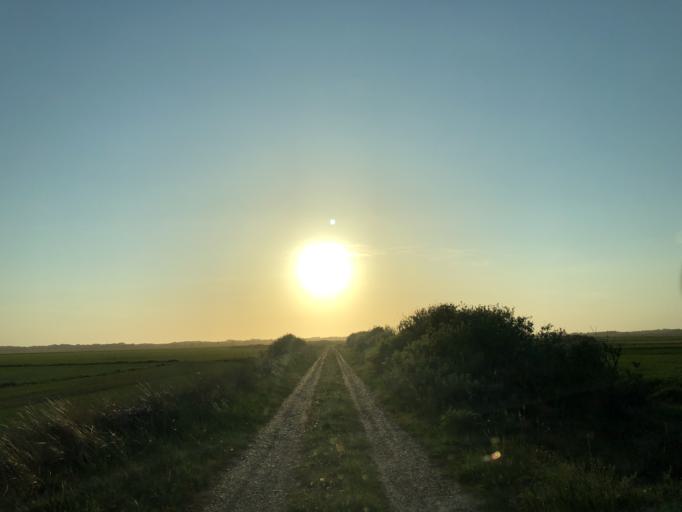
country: DK
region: Central Jutland
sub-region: Holstebro Kommune
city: Ulfborg
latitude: 56.2467
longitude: 8.1626
